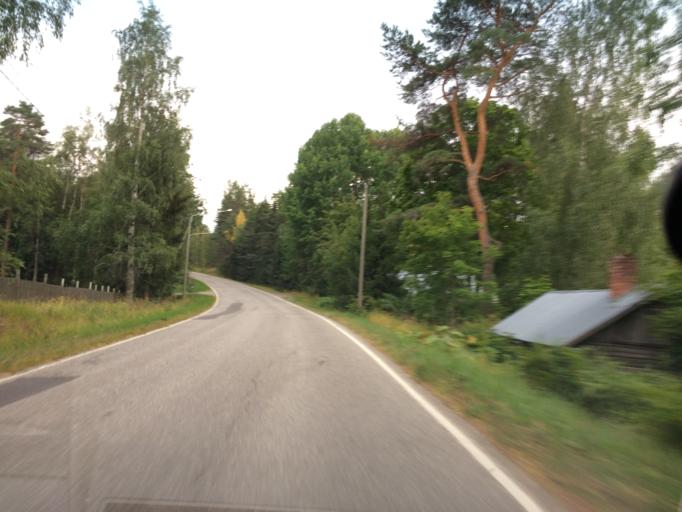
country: FI
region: Pirkanmaa
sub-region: Tampere
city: Luopioinen
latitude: 61.2535
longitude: 24.7063
